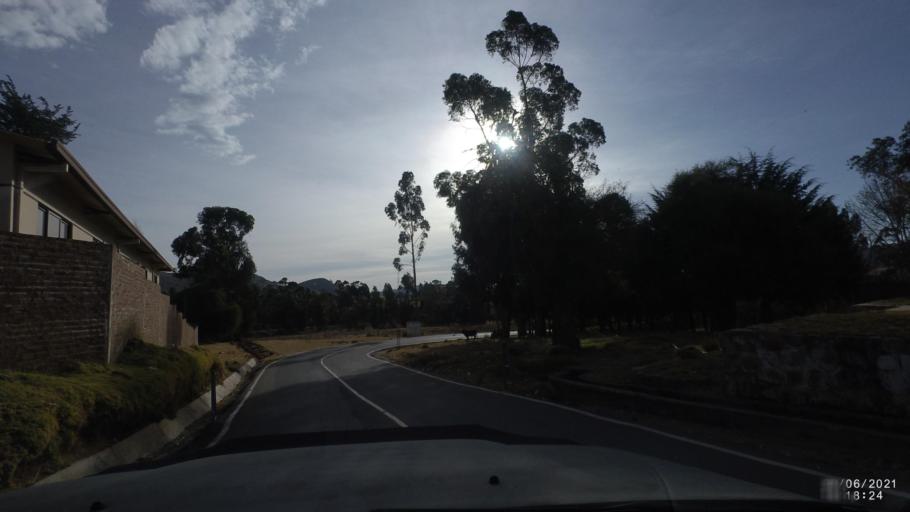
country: BO
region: Cochabamba
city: Arani
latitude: -17.8029
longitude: -65.8015
